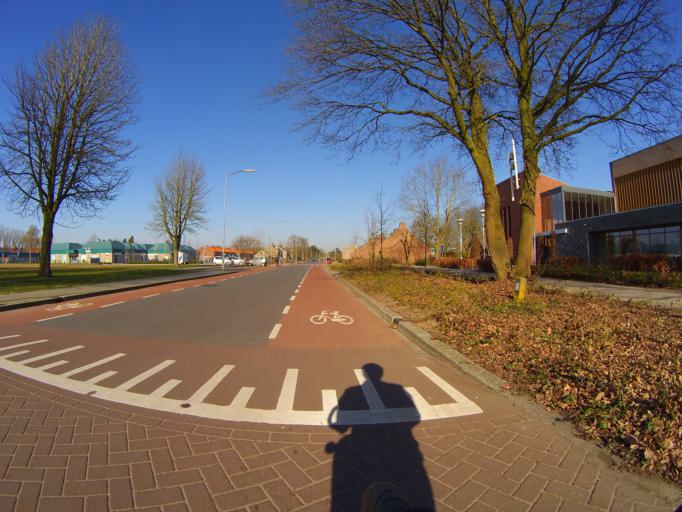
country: NL
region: Gelderland
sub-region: Gemeente Nijkerk
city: Nijkerk
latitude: 52.2140
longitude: 5.4908
